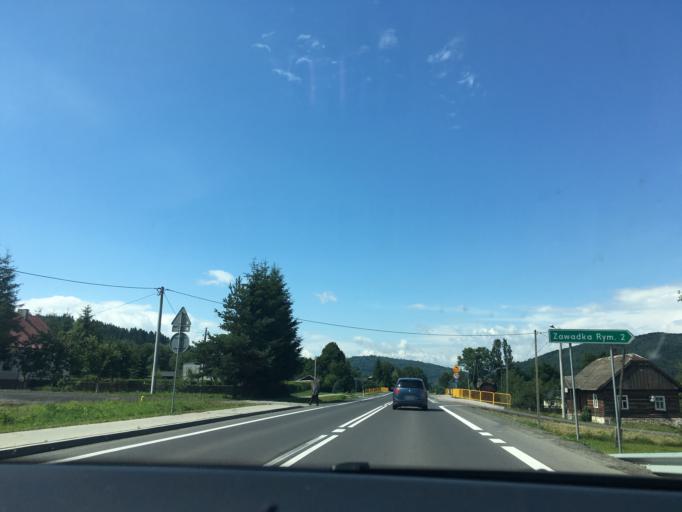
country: PL
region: Subcarpathian Voivodeship
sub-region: Powiat krosnienski
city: Dukla
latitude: 49.5002
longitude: 21.6998
